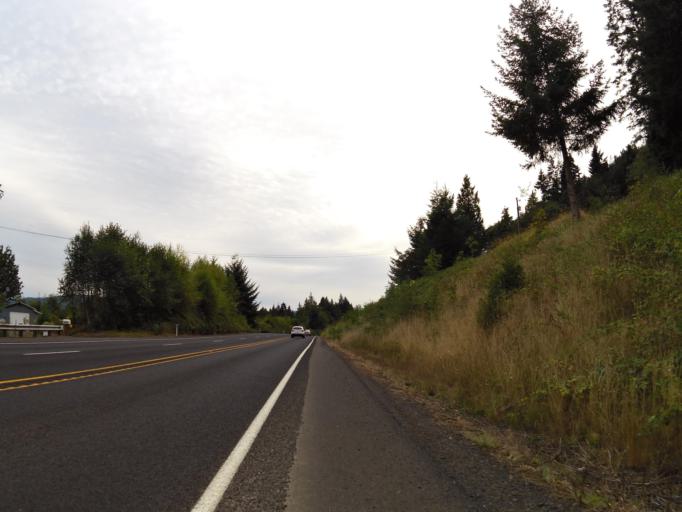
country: US
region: Oregon
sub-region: Columbia County
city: Clatskanie
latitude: 46.1625
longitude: -123.2524
